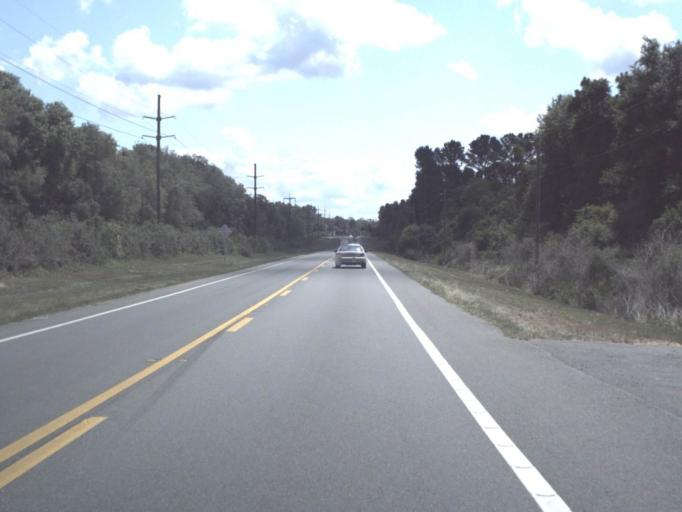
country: US
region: Florida
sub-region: Putnam County
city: Interlachen
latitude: 29.6163
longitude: -81.9741
